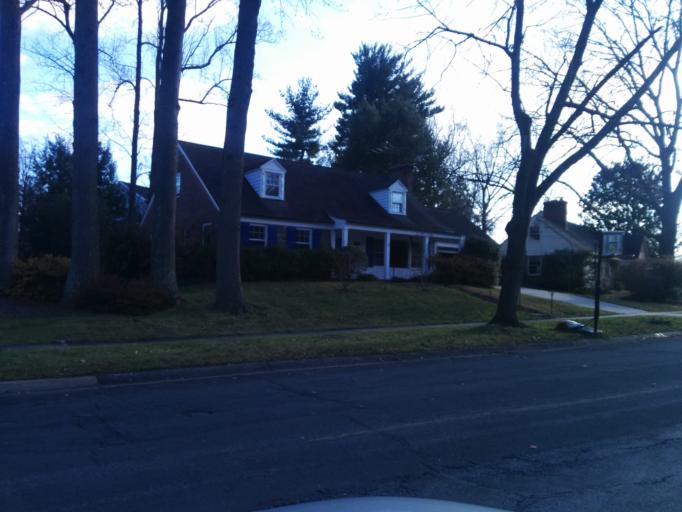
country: US
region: Maryland
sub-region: Montgomery County
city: Brookmont
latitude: 38.9557
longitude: -77.1179
